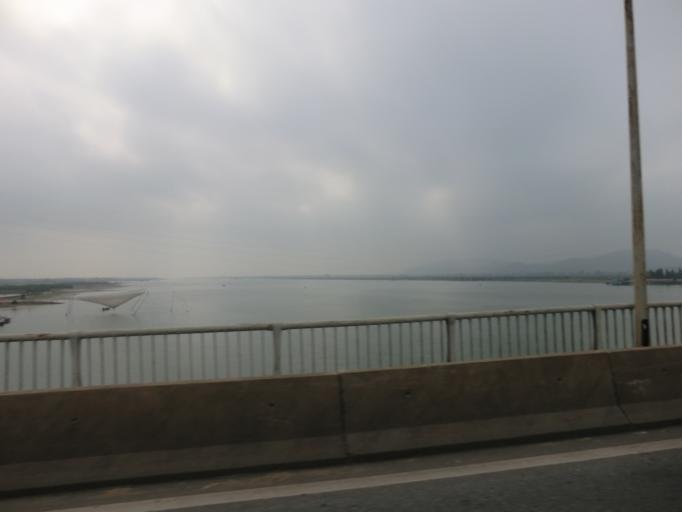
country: VN
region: Quang Binh
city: Ba Don
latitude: 17.7143
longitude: 106.4432
